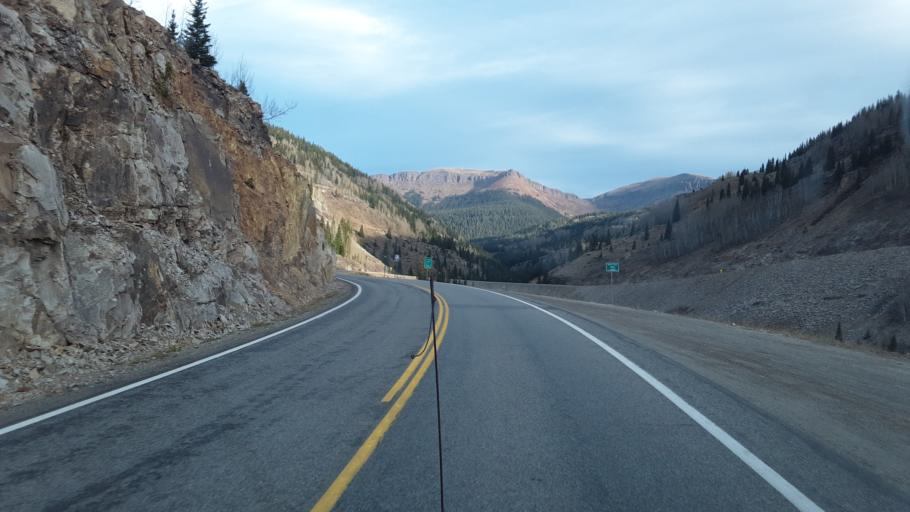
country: US
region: Colorado
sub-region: San Juan County
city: Silverton
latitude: 37.7261
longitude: -107.7492
